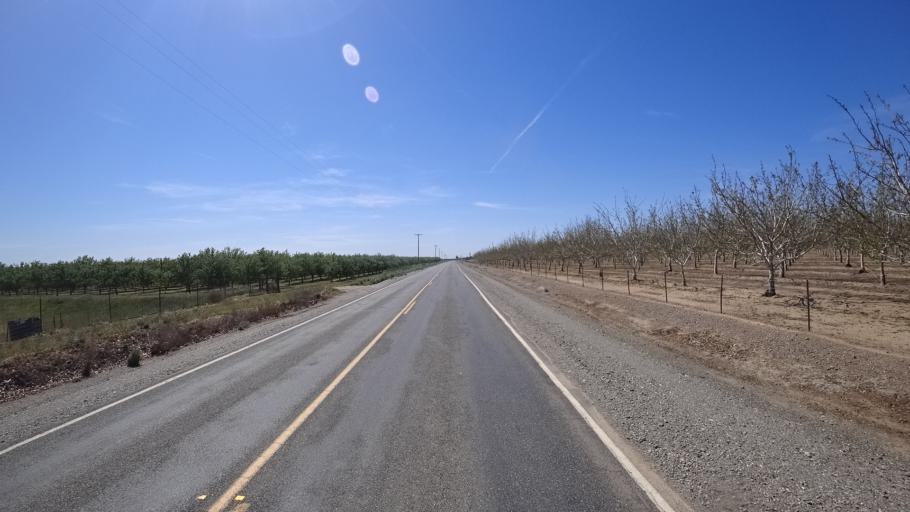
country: US
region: California
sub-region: Glenn County
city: Orland
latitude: 39.7019
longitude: -122.1405
